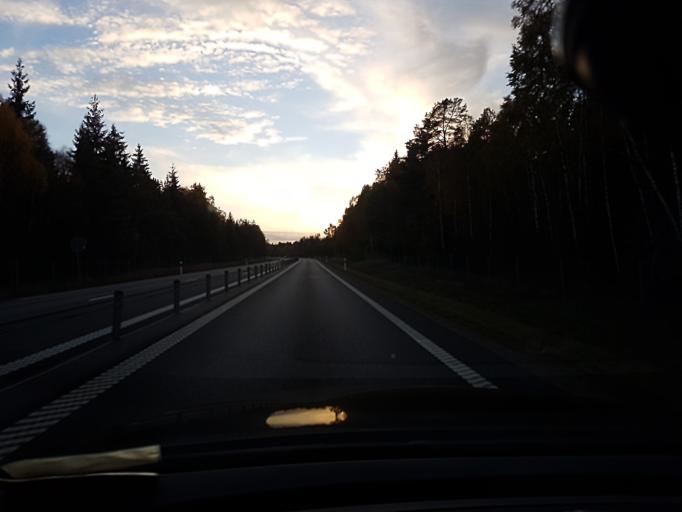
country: SE
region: Kronoberg
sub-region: Ljungby Kommun
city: Ljungby
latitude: 56.7893
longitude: 13.8373
